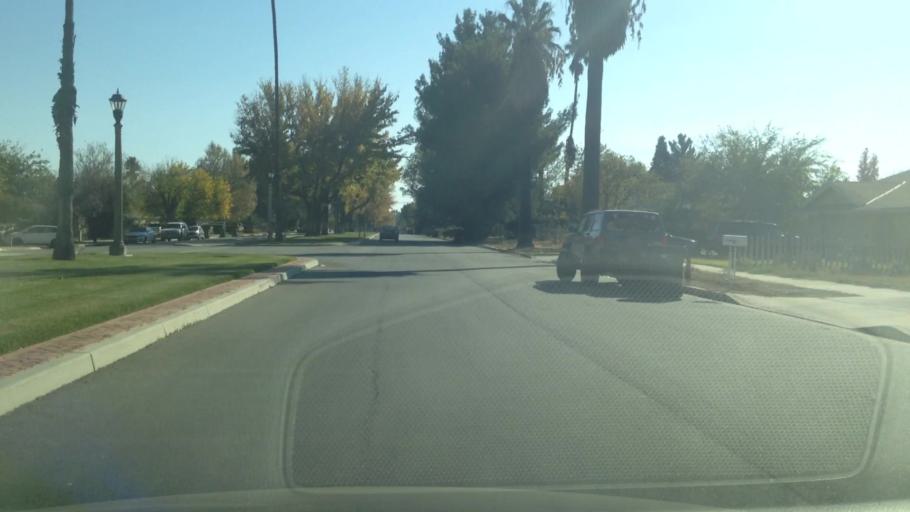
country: US
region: California
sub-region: Riverside County
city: Beaumont
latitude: 33.9391
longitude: -116.9718
